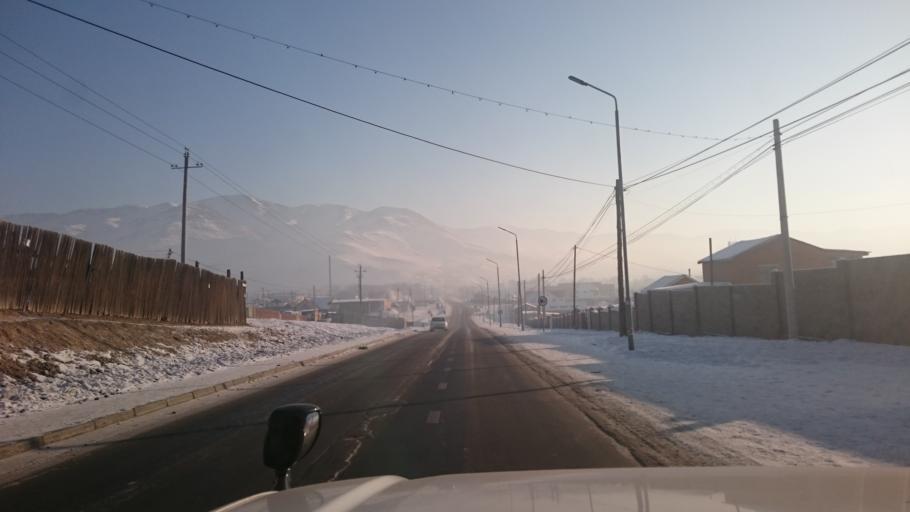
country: MN
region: Ulaanbaatar
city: Ulaanbaatar
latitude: 47.9291
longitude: 107.1511
